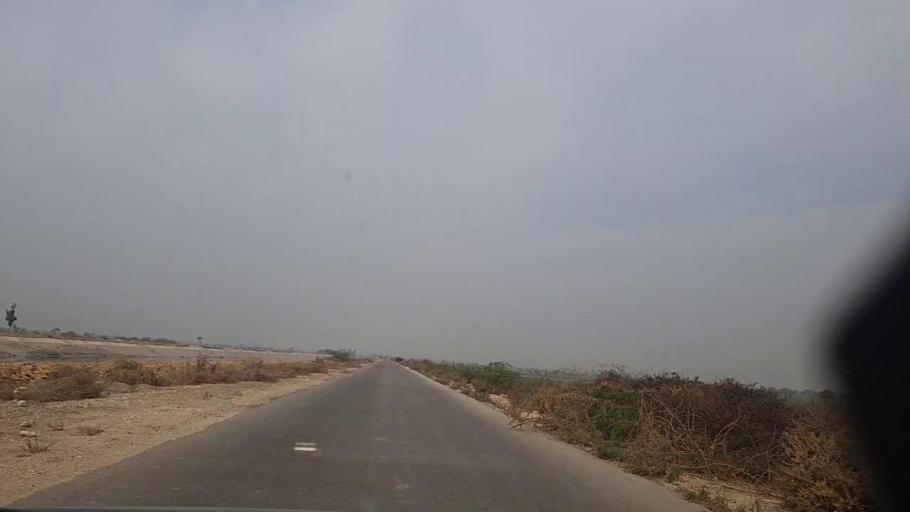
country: PK
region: Sindh
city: Sakrand
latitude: 26.2711
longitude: 68.2349
